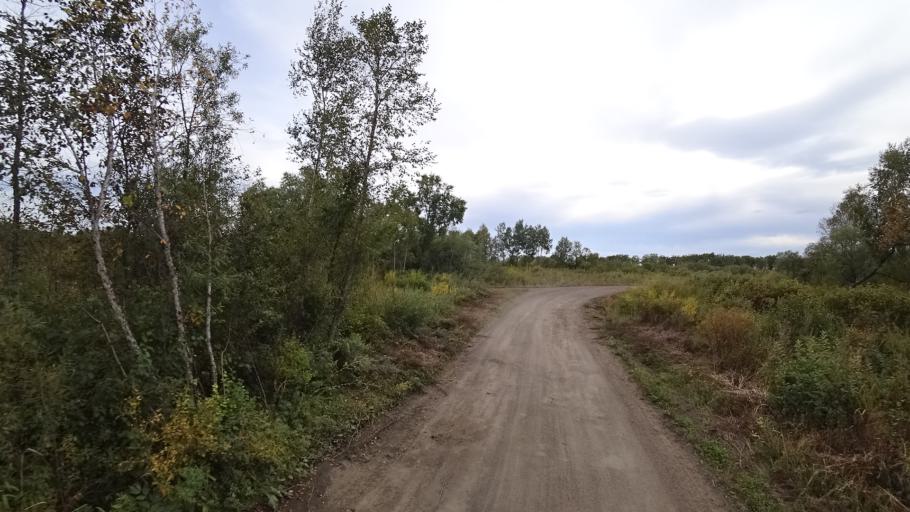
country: RU
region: Amur
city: Arkhara
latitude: 49.3516
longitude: 130.1549
